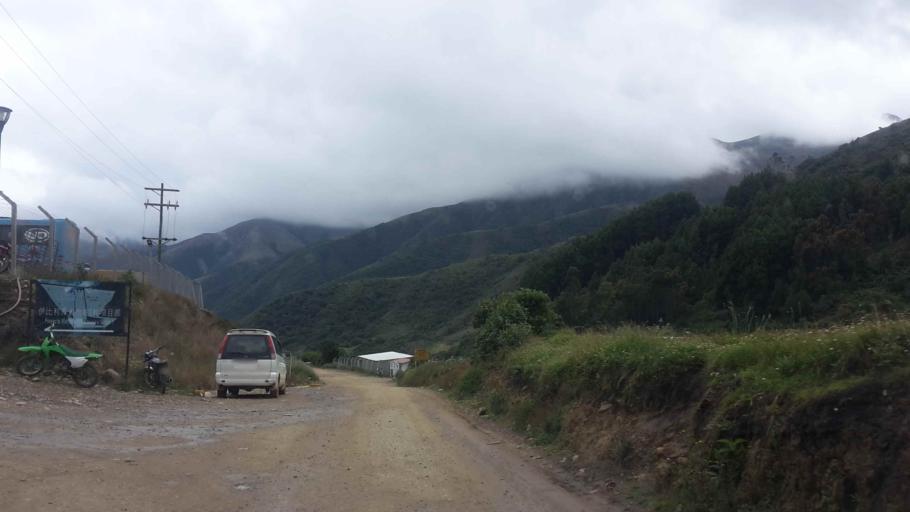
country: BO
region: Cochabamba
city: Totora
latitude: -17.5729
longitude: -65.2836
